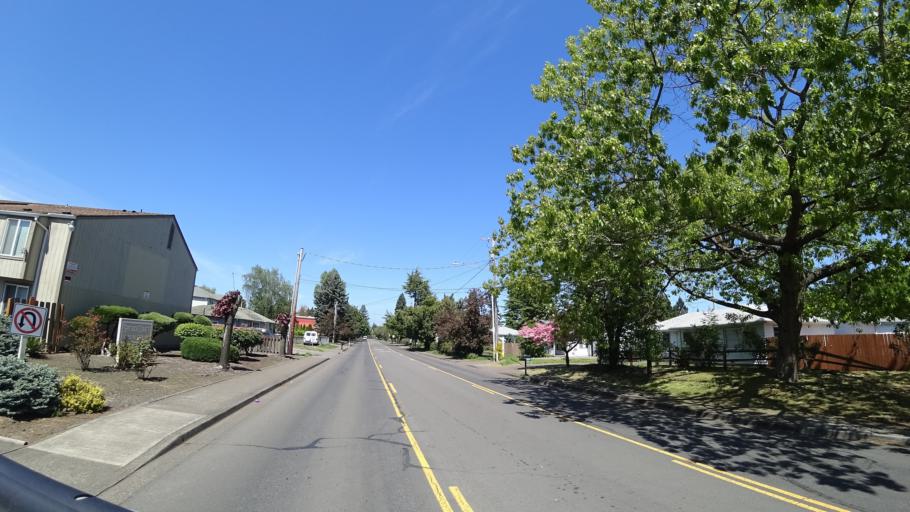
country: US
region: Oregon
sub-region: Washington County
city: Hillsboro
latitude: 45.5115
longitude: -122.9690
